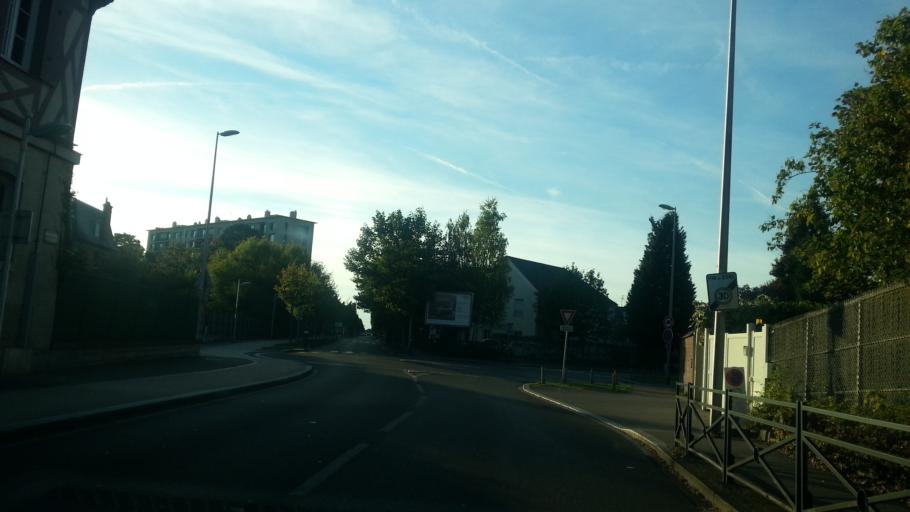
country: FR
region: Picardie
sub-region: Departement de l'Oise
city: Compiegne
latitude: 49.4063
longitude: 2.8335
